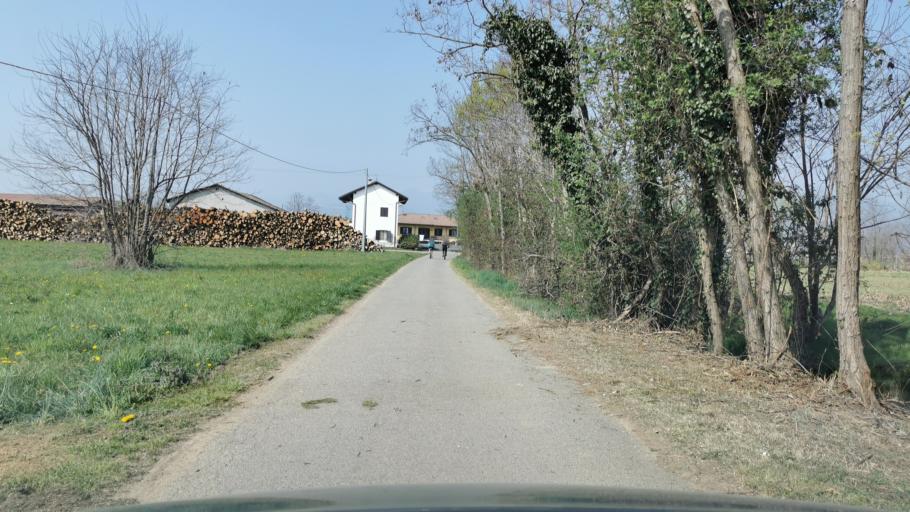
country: IT
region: Piedmont
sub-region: Provincia di Torino
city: Favria
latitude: 45.3226
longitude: 7.6988
